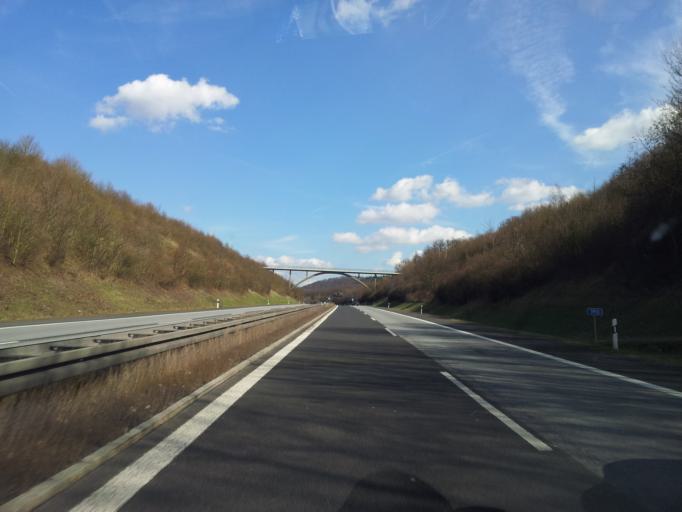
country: DE
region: Bavaria
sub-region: Regierungsbezirk Unterfranken
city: Sand
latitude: 49.9748
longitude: 10.5806
